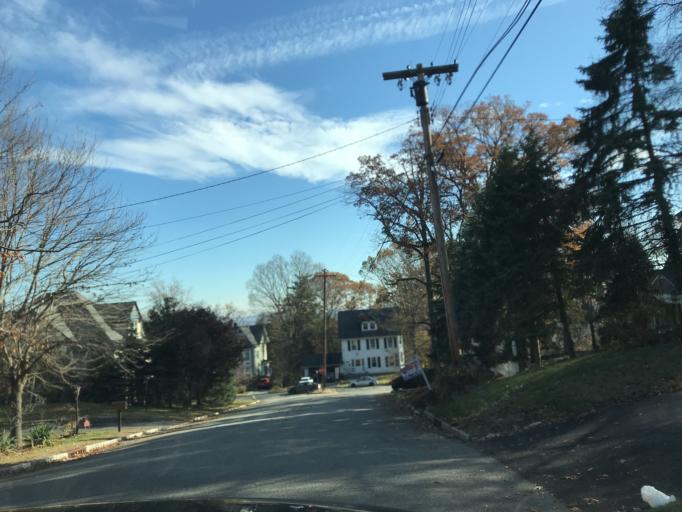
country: US
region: New Jersey
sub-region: Morris County
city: Boonton
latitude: 40.9016
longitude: -74.4162
